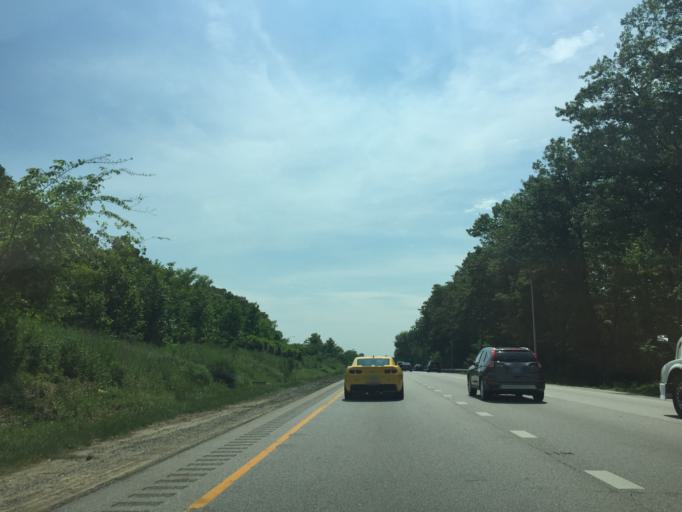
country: US
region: Maryland
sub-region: Howard County
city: Elkridge
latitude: 39.2091
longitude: -76.6848
